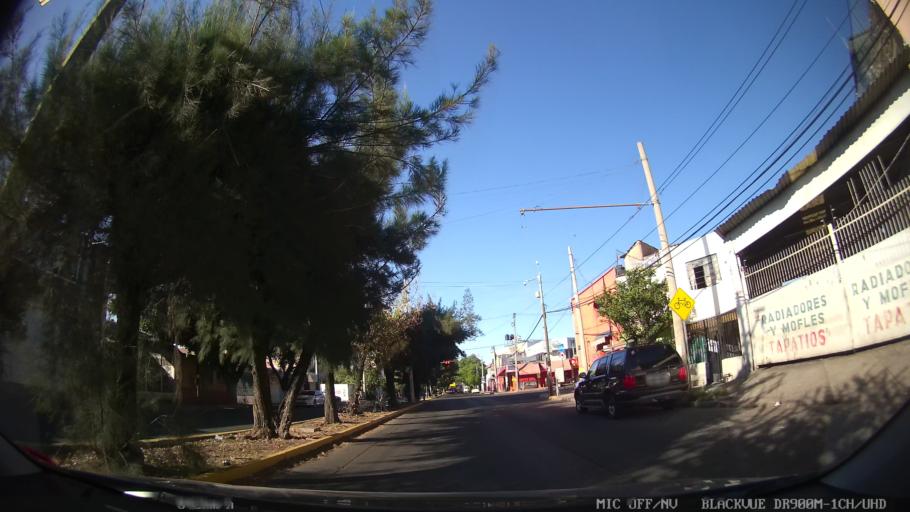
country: MX
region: Jalisco
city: Tlaquepaque
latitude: 20.6846
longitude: -103.3246
